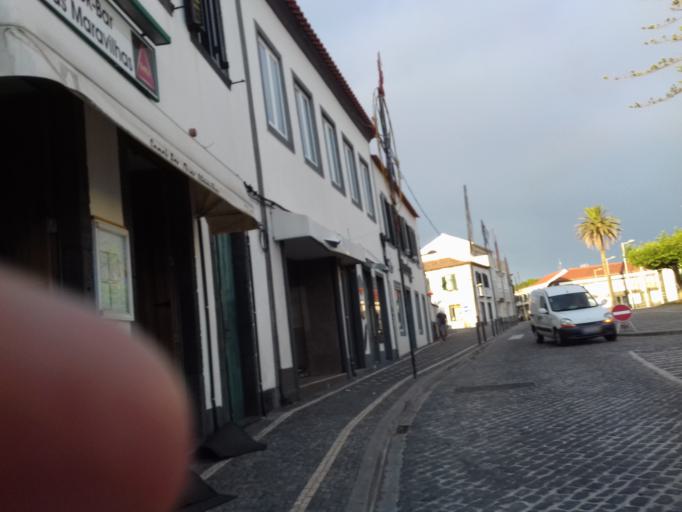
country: PT
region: Azores
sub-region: Madalena
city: Madalena
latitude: 38.5347
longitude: -28.5283
